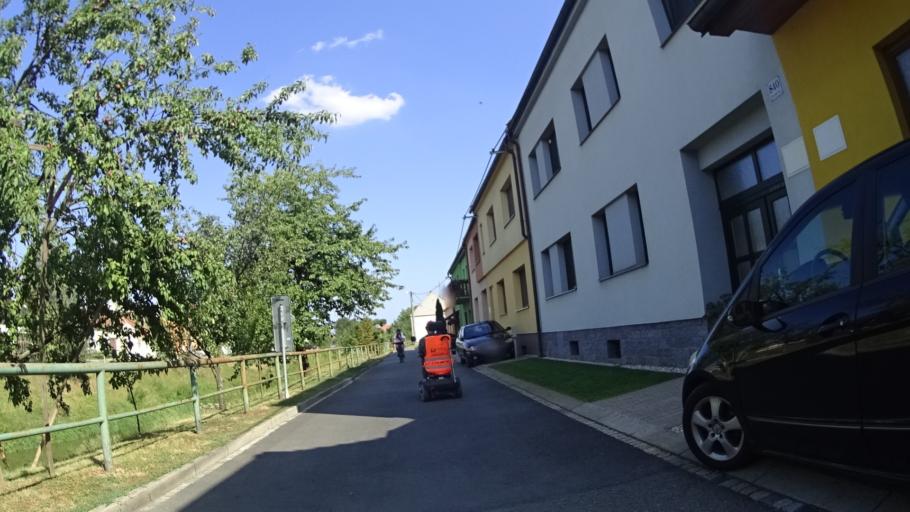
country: CZ
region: Zlin
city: Kunovice
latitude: 49.0462
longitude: 17.4640
